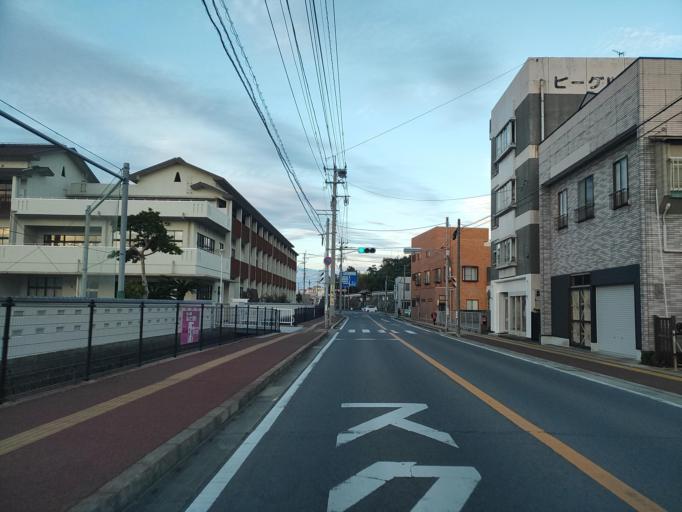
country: JP
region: Nagasaki
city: Fukuecho
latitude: 32.6921
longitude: 128.8430
